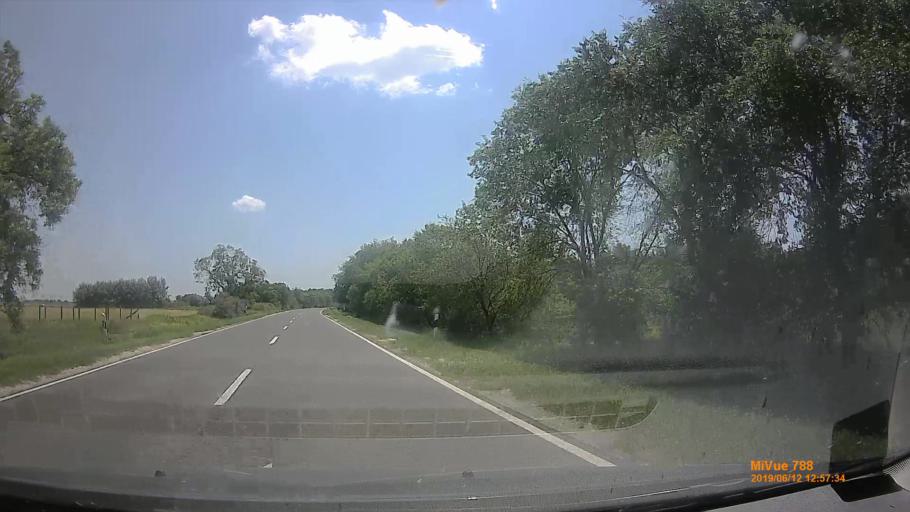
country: HU
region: Bacs-Kiskun
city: Palmonostora
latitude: 46.6337
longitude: 19.8931
